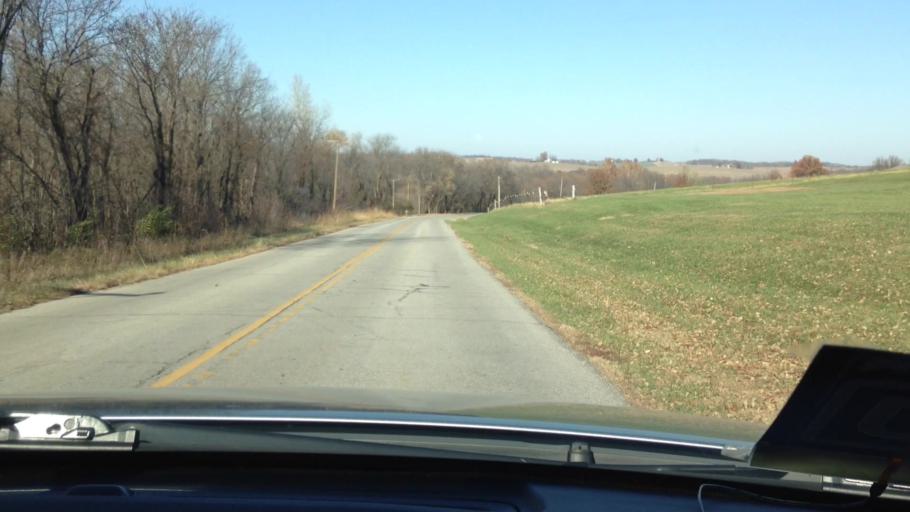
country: US
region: Missouri
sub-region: Platte County
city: Weston
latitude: 39.4439
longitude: -94.8544
